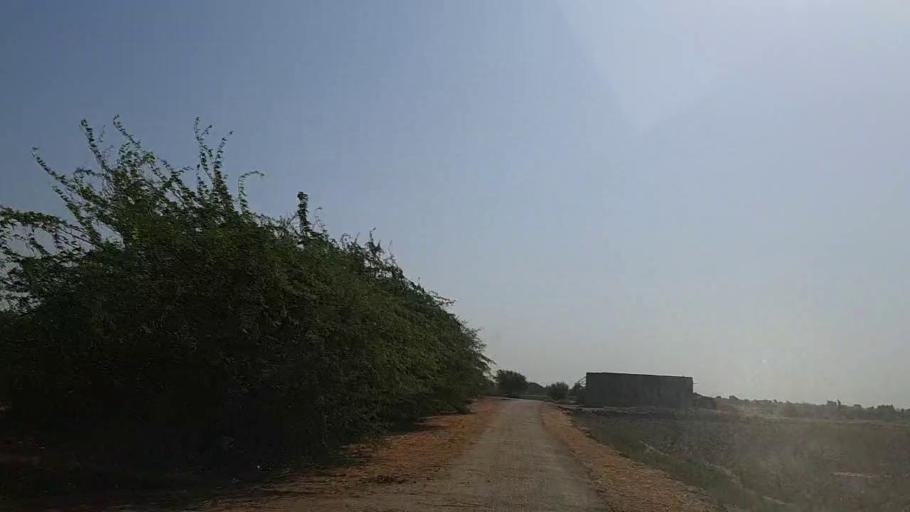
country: PK
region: Sindh
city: Daro Mehar
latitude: 24.7193
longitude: 68.1145
